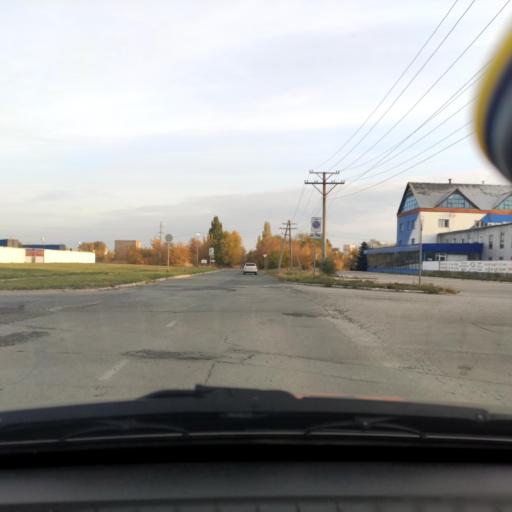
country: RU
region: Samara
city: Tol'yatti
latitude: 53.5531
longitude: 49.3234
